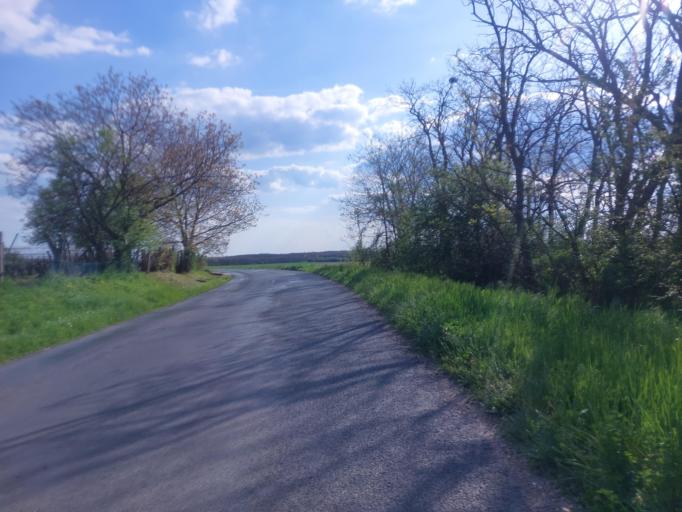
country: HU
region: Veszprem
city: Devecser
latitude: 47.1554
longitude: 17.3586
